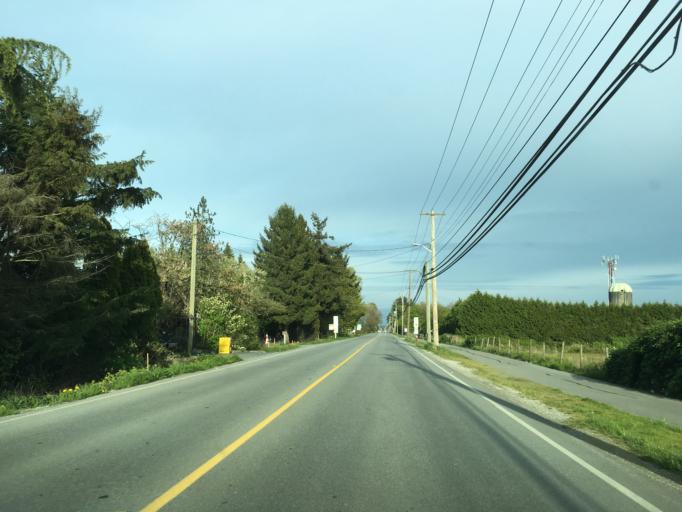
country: CA
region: British Columbia
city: Richmond
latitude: 49.1699
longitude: -123.0633
